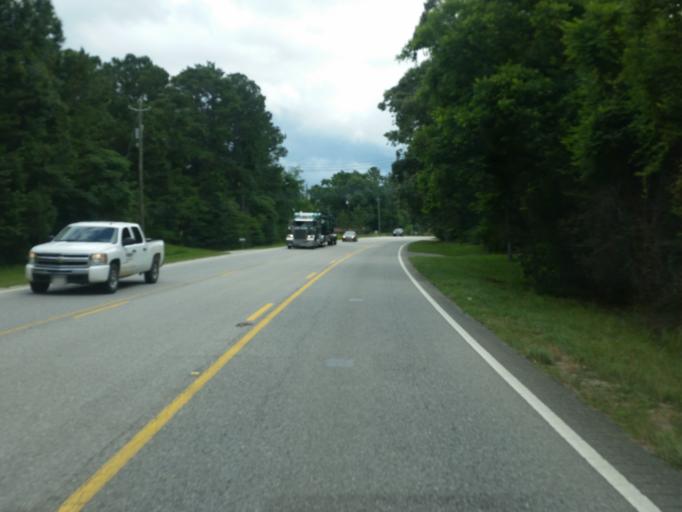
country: US
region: Mississippi
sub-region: George County
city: Lucedale
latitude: 30.8490
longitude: -88.3983
